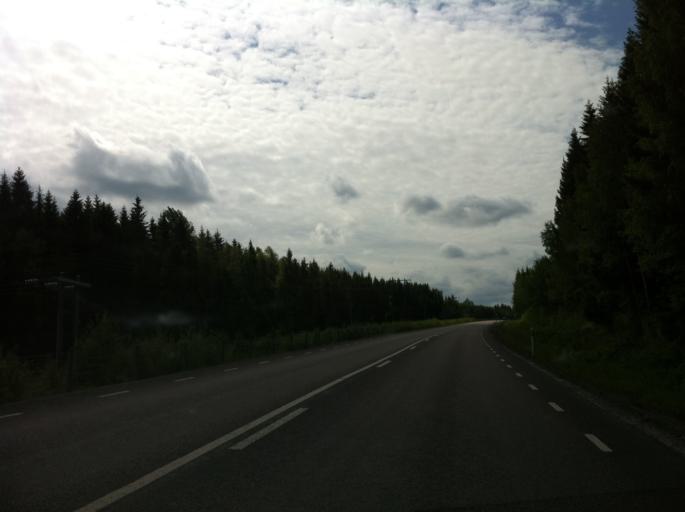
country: SE
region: Vaermland
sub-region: Karlstads Kommun
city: Edsvalla
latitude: 59.4415
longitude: 13.2025
